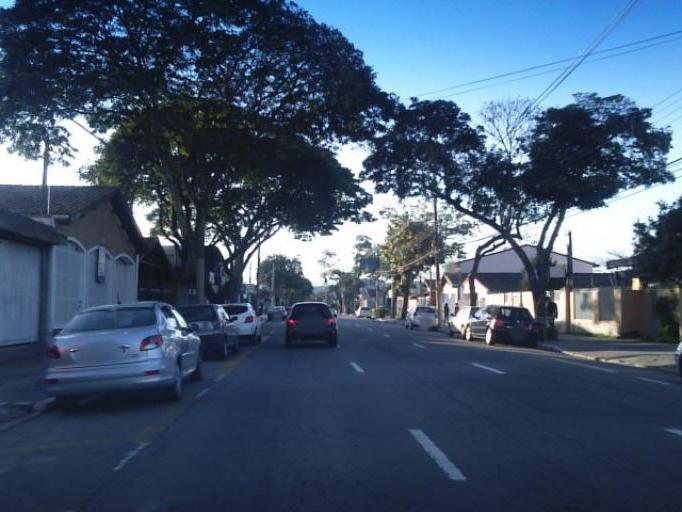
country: BR
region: Sao Paulo
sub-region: Sao Jose Dos Campos
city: Sao Jose dos Campos
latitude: -23.1638
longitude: -45.8925
